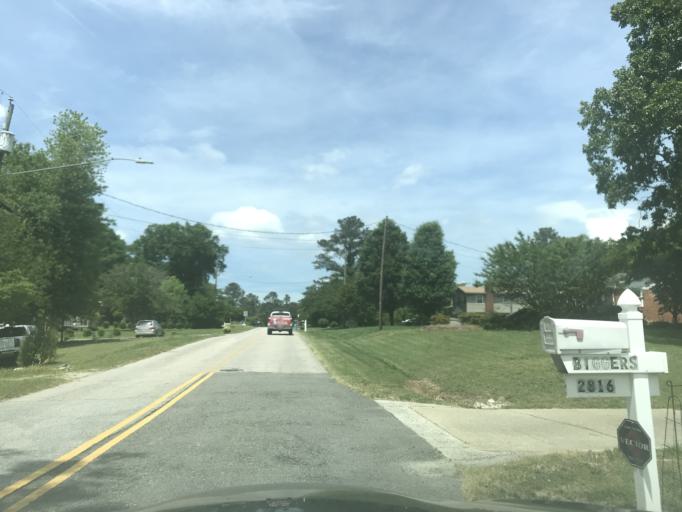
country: US
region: North Carolina
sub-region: Wake County
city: Raleigh
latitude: 35.8196
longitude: -78.5805
